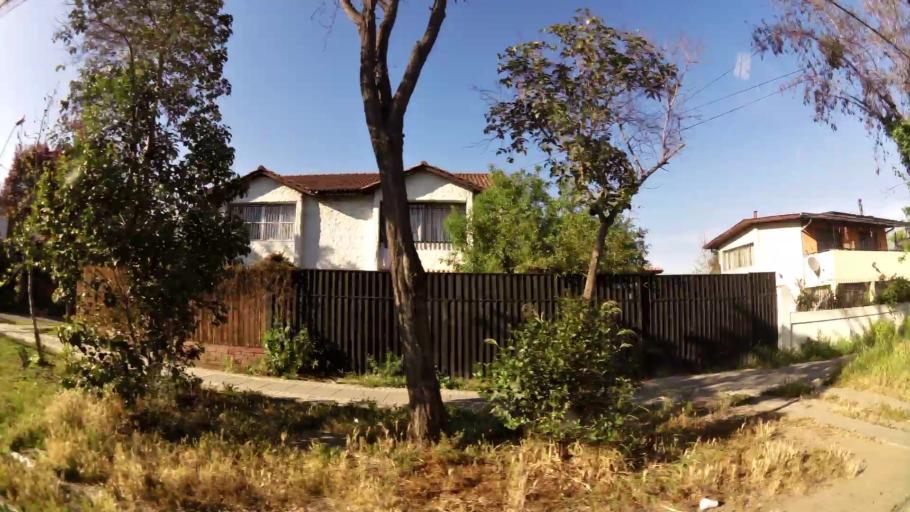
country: CL
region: Santiago Metropolitan
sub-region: Provincia de Santiago
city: Villa Presidente Frei, Nunoa, Santiago, Chile
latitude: -33.4548
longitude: -70.5620
